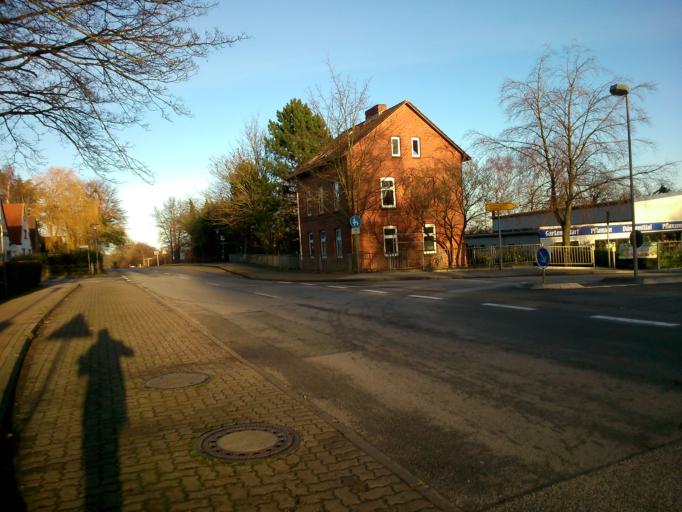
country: DE
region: Schleswig-Holstein
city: Lutjenburg
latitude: 54.2958
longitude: 10.5951
